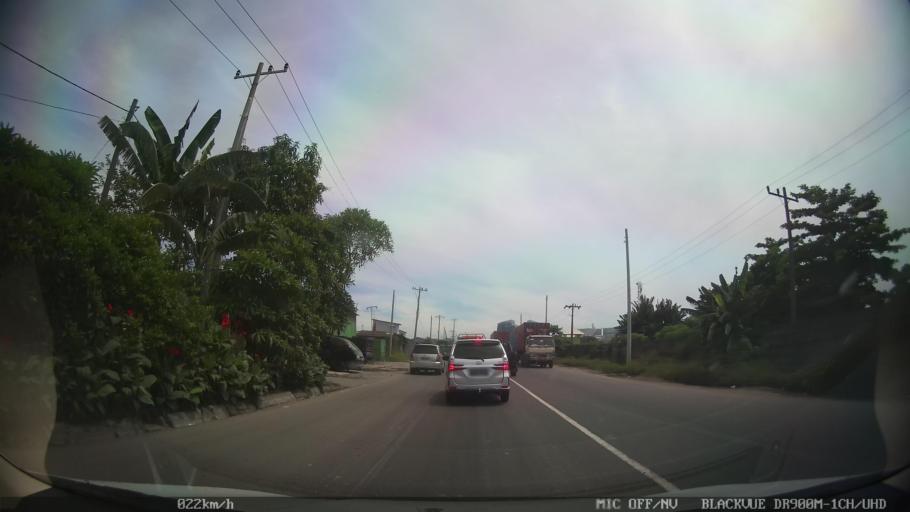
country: ID
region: North Sumatra
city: Belawan
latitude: 3.7763
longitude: 98.6866
